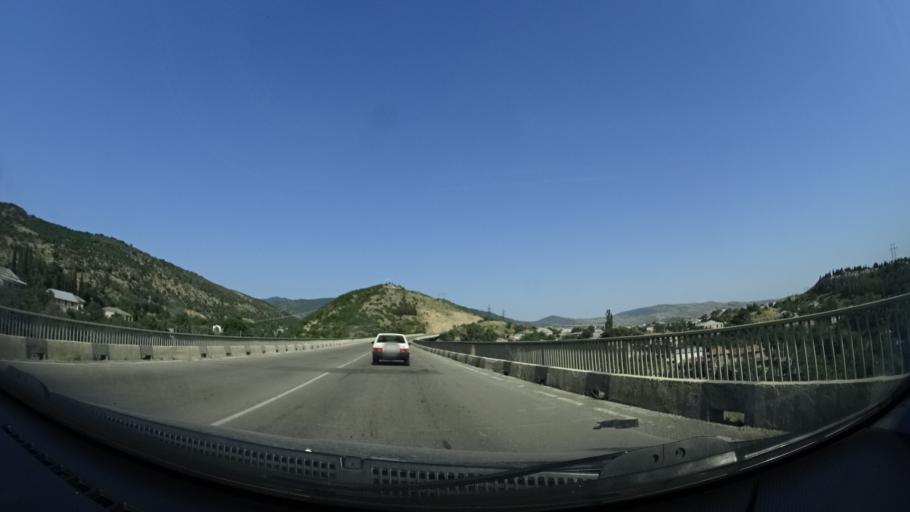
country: GE
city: Zahesi
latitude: 41.8248
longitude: 44.8247
